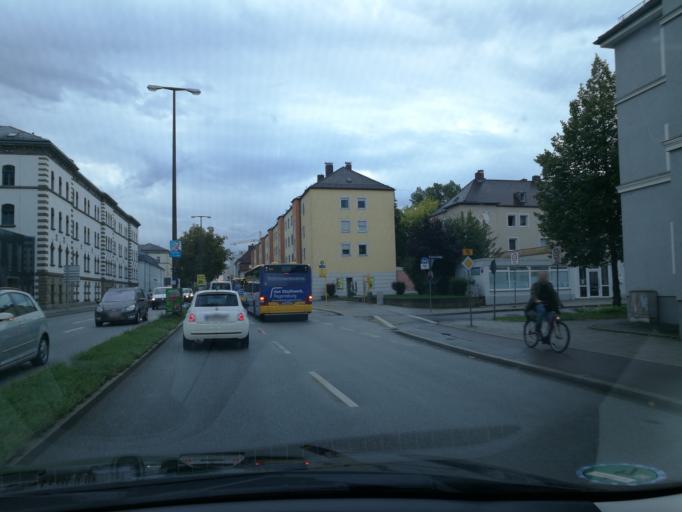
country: DE
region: Bavaria
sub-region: Upper Palatinate
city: Regensburg
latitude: 49.0085
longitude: 12.1148
